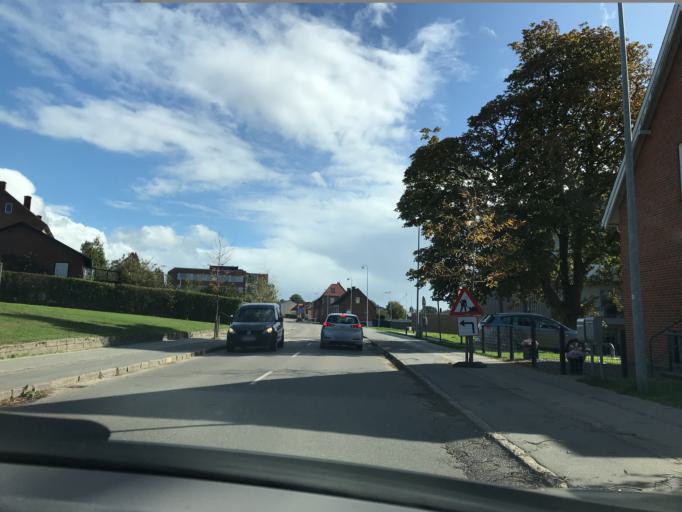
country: DK
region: Central Jutland
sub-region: Skanderborg Kommune
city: Skanderborg
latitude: 56.0336
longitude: 9.9248
